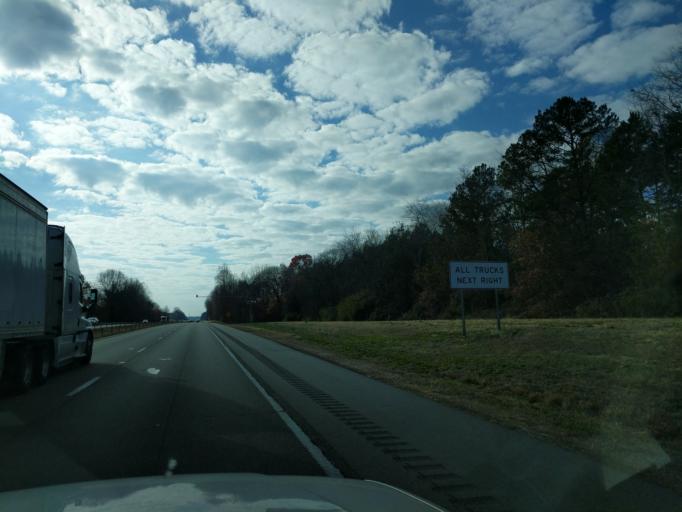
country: US
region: North Carolina
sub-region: Alexander County
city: Stony Point
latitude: 35.7715
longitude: -81.0015
